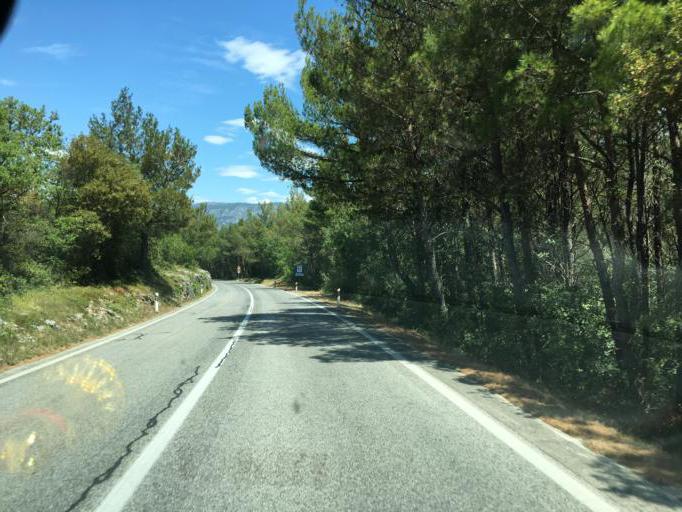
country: HR
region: Istarska
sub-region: Grad Labin
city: Labin
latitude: 45.1499
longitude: 14.1552
